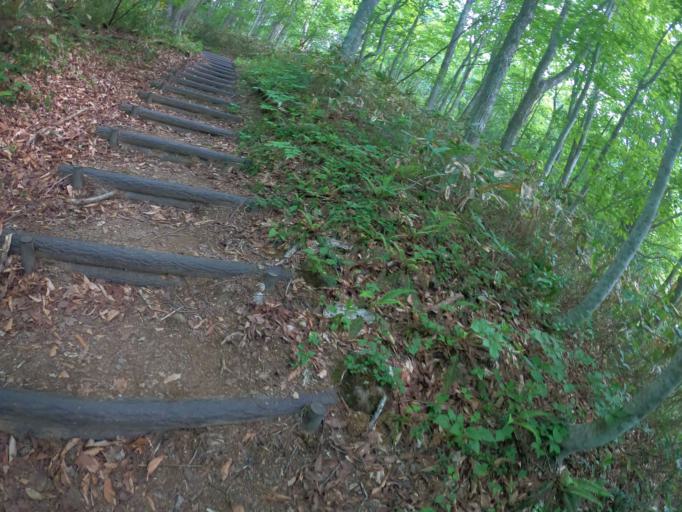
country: JP
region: Iwate
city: Ichinoseki
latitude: 38.9106
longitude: 140.8110
